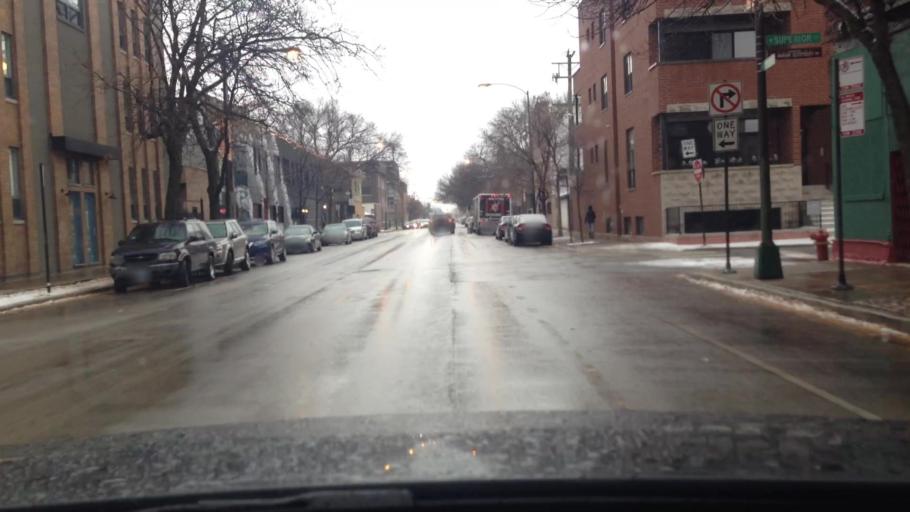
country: US
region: Illinois
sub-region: Cook County
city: Chicago
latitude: 41.8951
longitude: -87.6771
